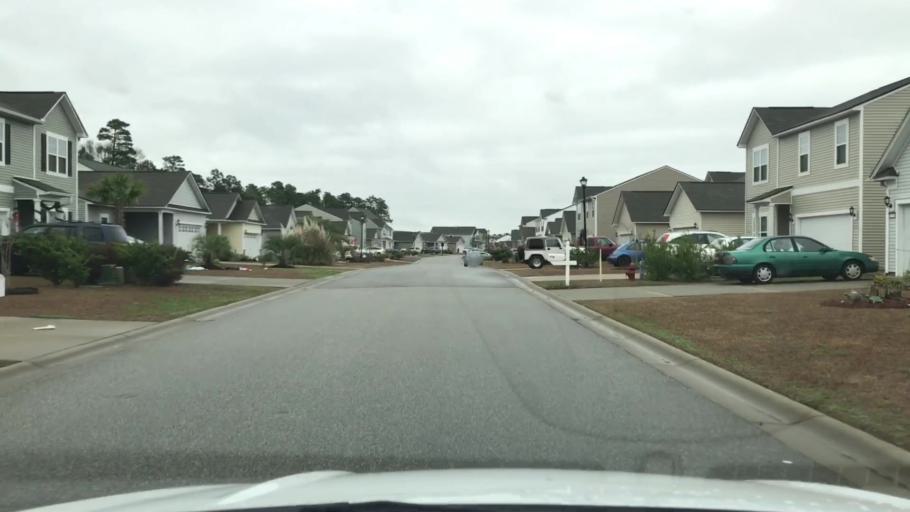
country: US
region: South Carolina
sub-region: Horry County
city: Forestbrook
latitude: 33.7467
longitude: -78.9075
